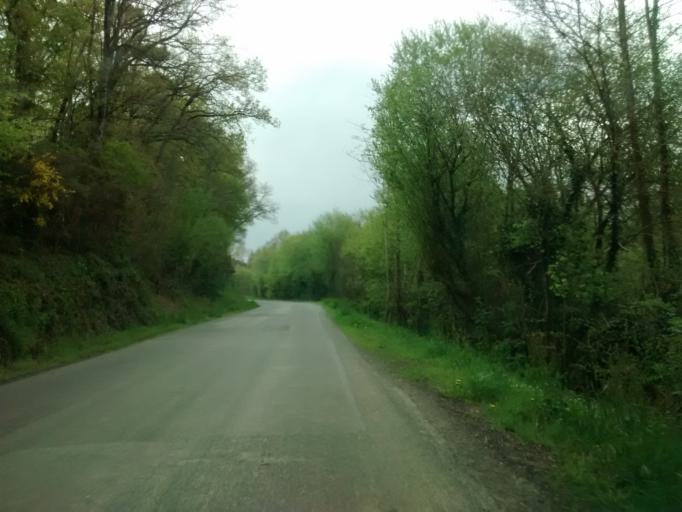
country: FR
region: Brittany
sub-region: Departement du Morbihan
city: Ruffiac
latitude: 47.7829
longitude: -2.3147
